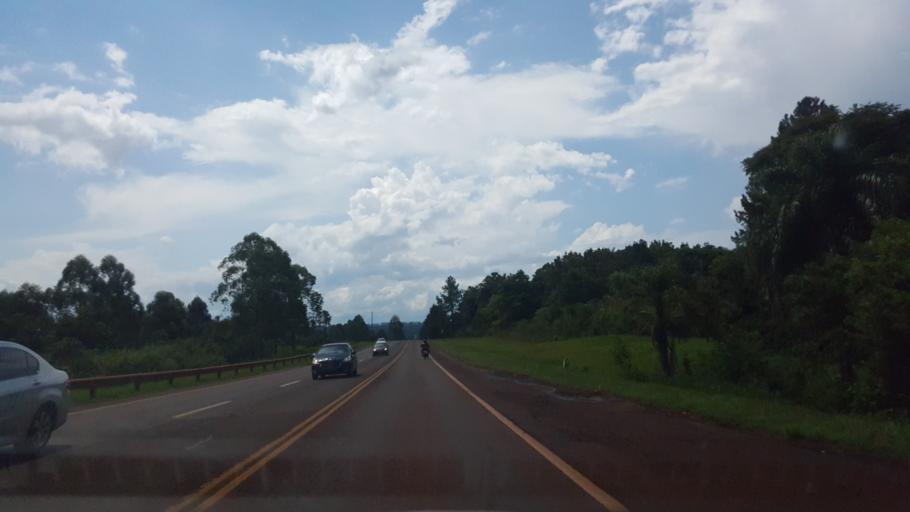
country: AR
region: Misiones
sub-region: Departamento de Eldorado
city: Eldorado
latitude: -26.3236
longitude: -54.6153
